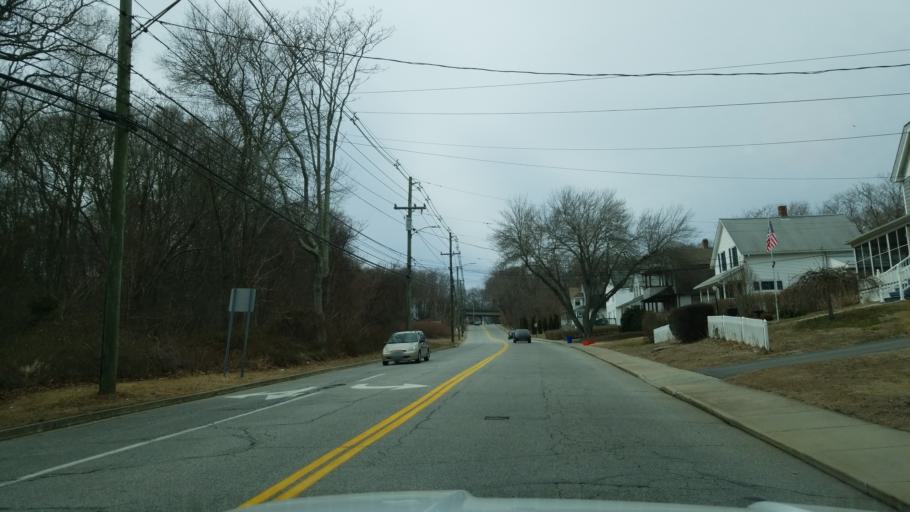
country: US
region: Connecticut
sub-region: New London County
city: Groton
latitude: 41.3442
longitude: -72.0653
